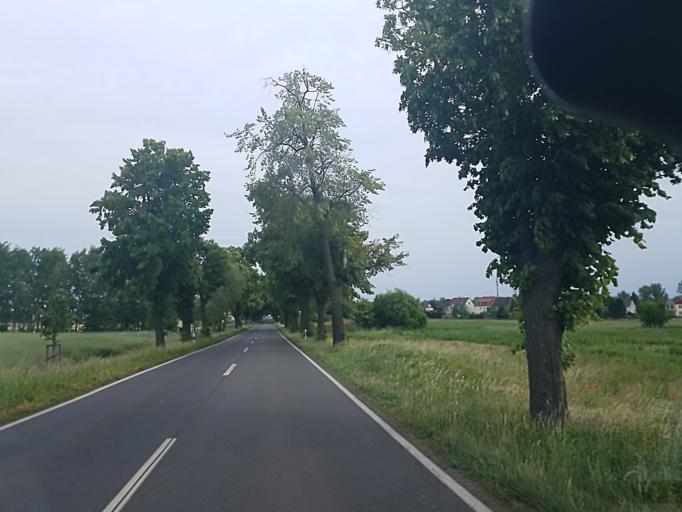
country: DE
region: Saxony-Anhalt
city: Wittenburg
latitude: 51.8829
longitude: 12.6287
